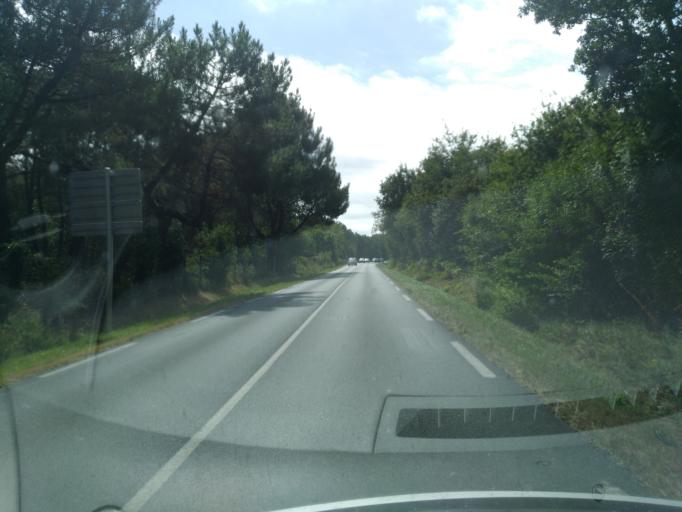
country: FR
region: Poitou-Charentes
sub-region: Departement de la Charente-Maritime
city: Chaillevette
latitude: 45.7182
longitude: -1.0723
